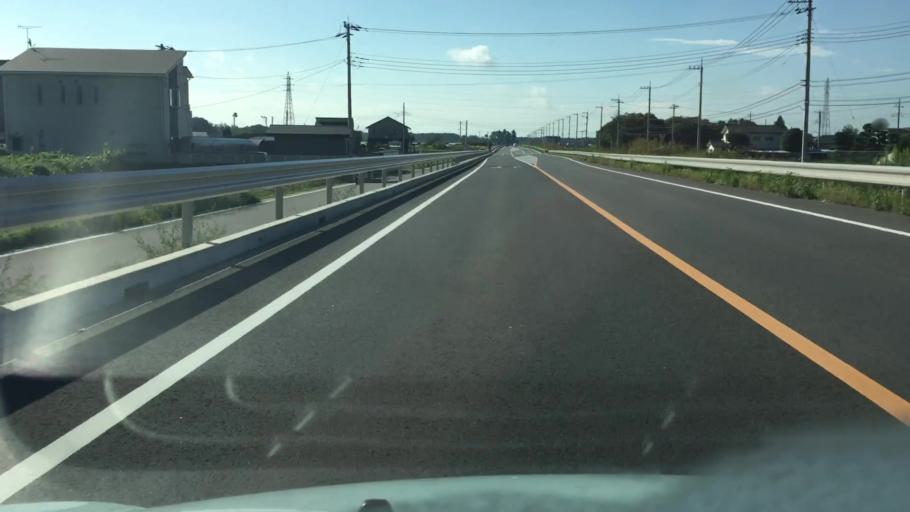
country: JP
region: Tochigi
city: Ujiie
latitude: 36.6039
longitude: 139.9840
